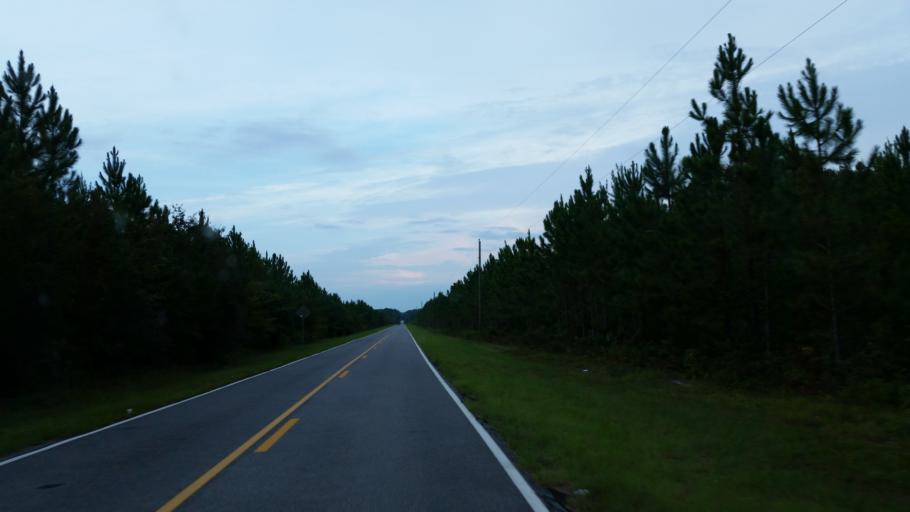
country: US
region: Georgia
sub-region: Lowndes County
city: Valdosta
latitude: 30.7456
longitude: -83.2514
